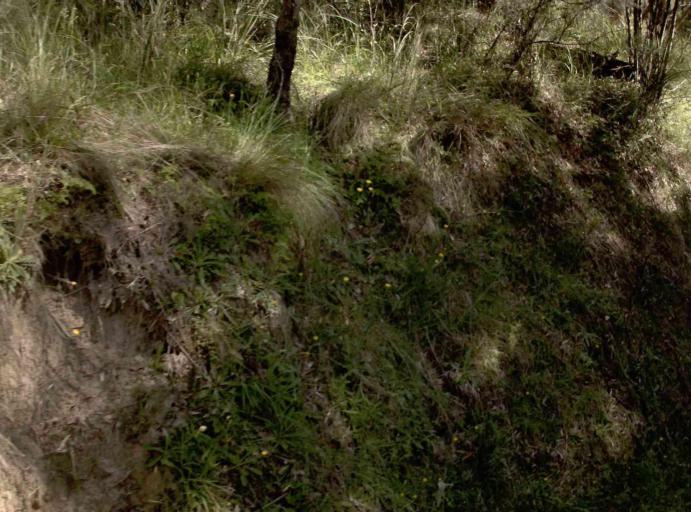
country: AU
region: New South Wales
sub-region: Bombala
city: Bombala
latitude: -37.3661
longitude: 148.6825
